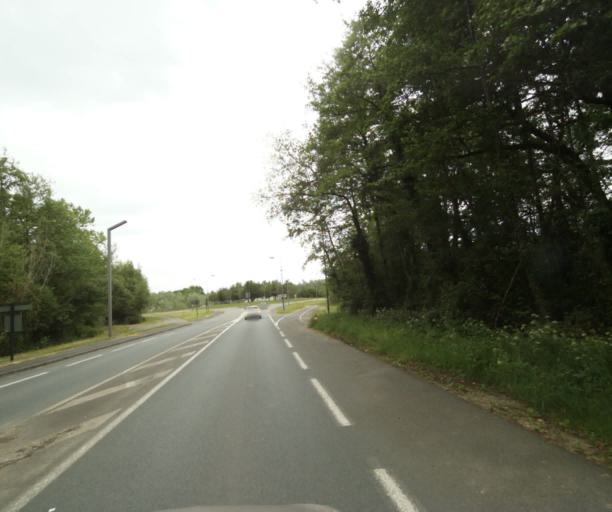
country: FR
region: Aquitaine
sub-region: Departement des Pyrenees-Atlantiques
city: Mouguerre
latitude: 43.4739
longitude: -1.4424
